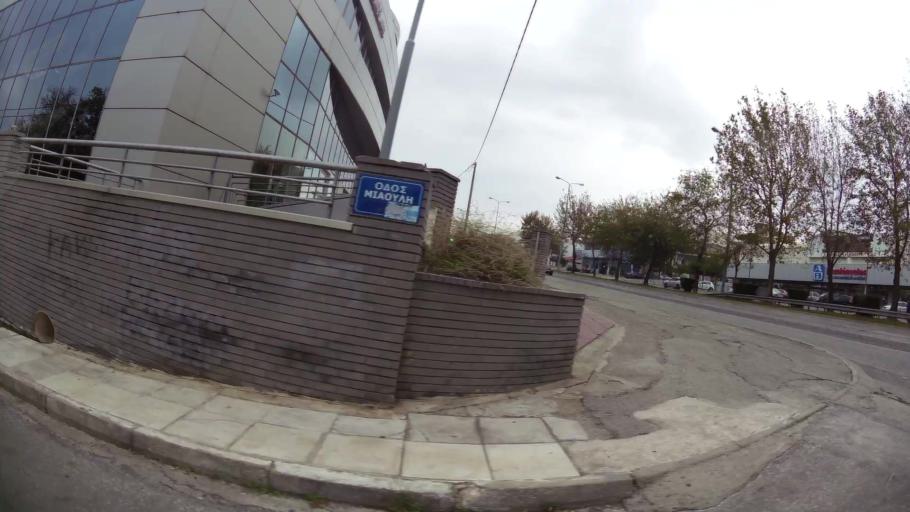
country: GR
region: Attica
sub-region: Nomarchia Athinas
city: Chaidari
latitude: 38.0124
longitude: 23.6644
